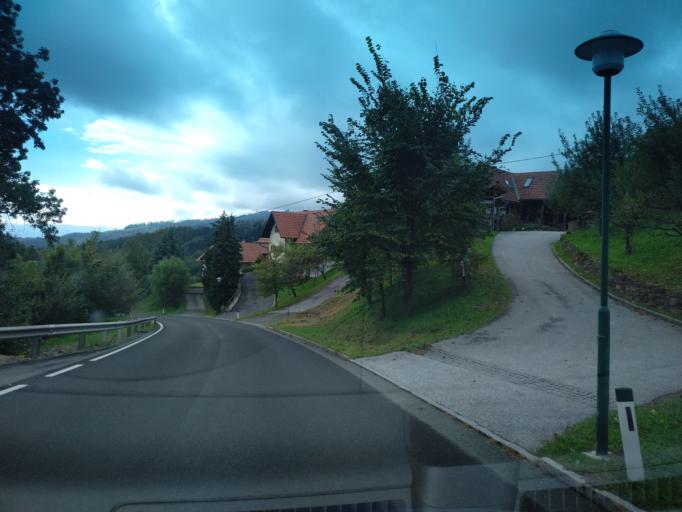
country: AT
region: Styria
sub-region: Politischer Bezirk Deutschlandsberg
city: Deutschlandsberg
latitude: 46.8270
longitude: 15.1995
